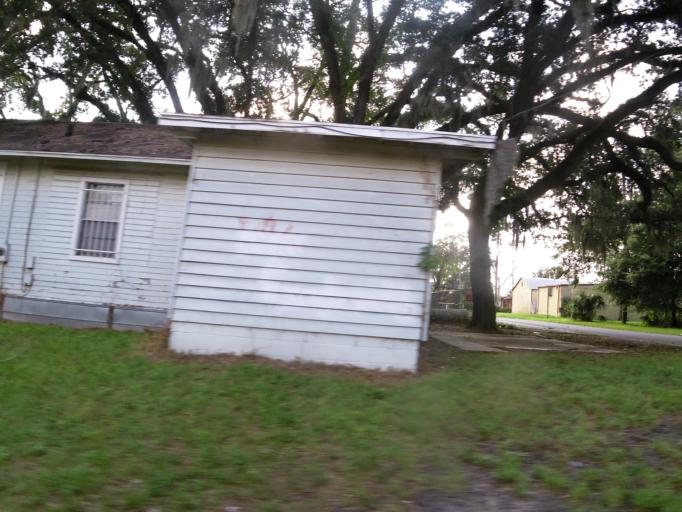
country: US
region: Florida
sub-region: Duval County
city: Jacksonville
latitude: 30.3299
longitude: -81.6898
